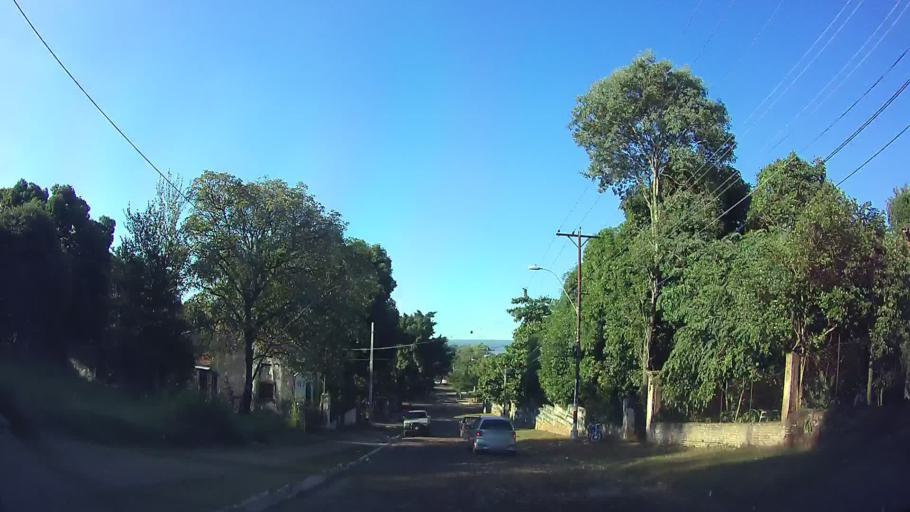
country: PY
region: Central
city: Aregua
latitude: -25.3128
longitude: -57.3839
